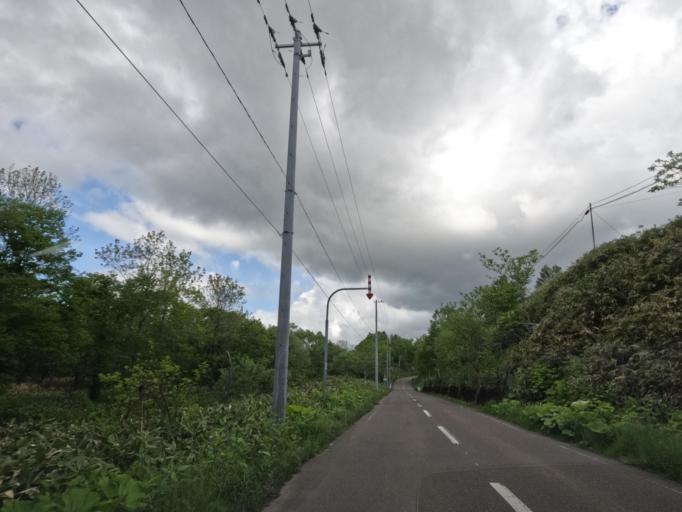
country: JP
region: Hokkaido
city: Tobetsu
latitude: 43.4597
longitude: 141.5940
